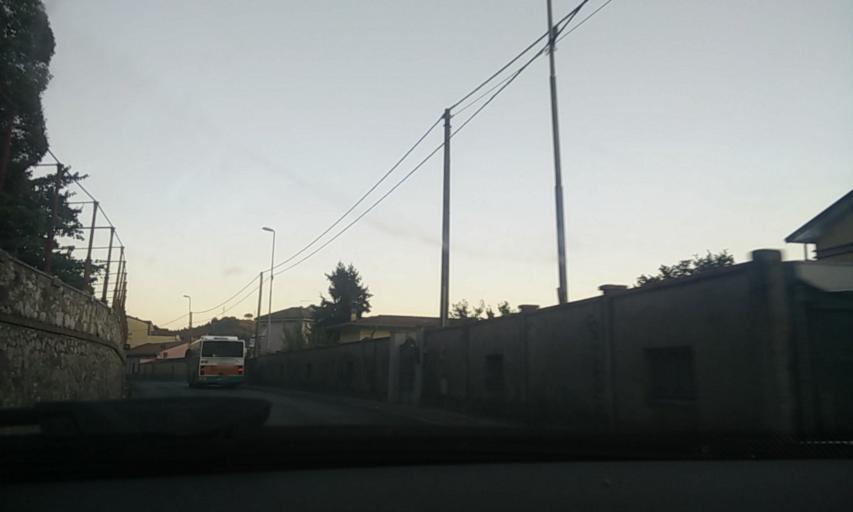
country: IT
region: Tuscany
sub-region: Provincia di Massa-Carrara
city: Carrara
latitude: 44.0662
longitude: 10.0830
